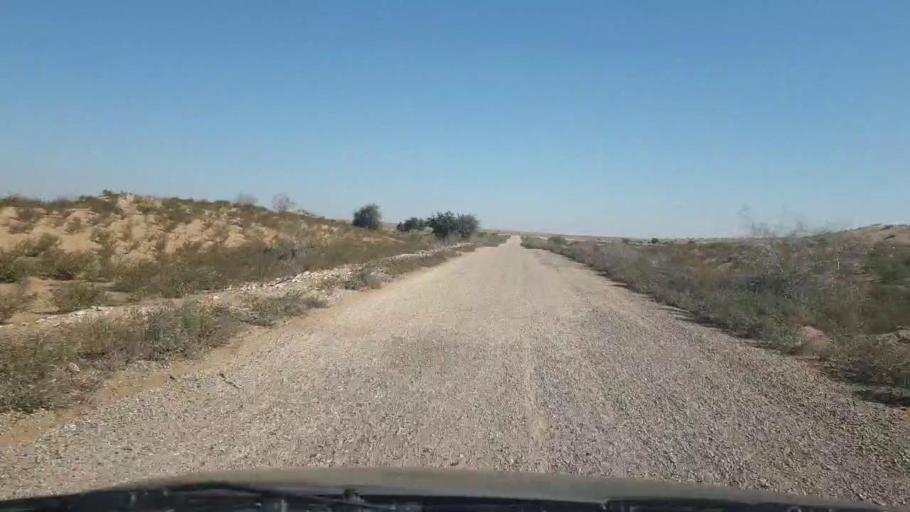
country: PK
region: Sindh
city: Bozdar
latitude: 27.0163
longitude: 68.7544
